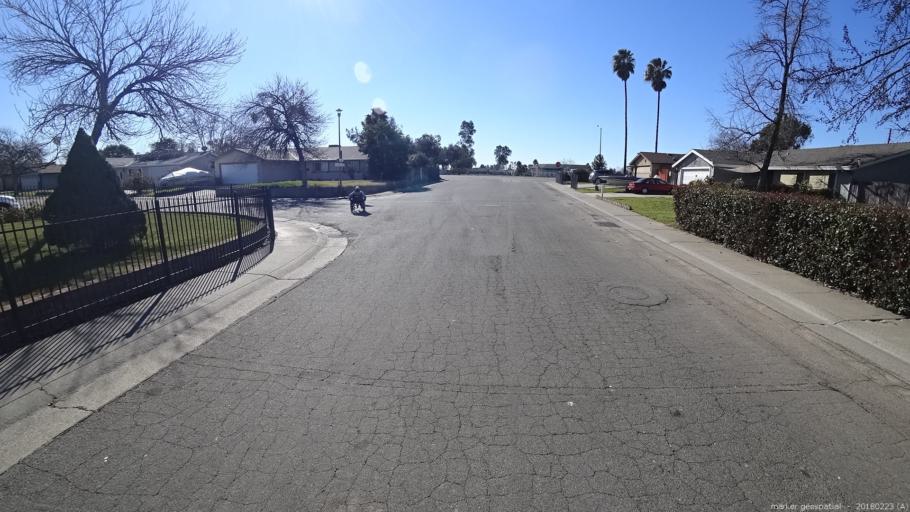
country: US
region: California
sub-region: Sacramento County
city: North Highlands
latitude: 38.7048
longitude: -121.3855
